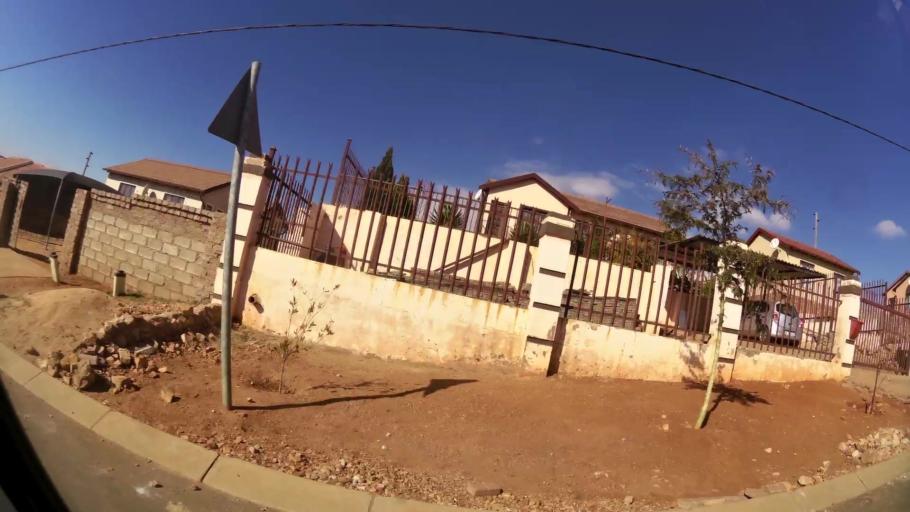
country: ZA
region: Gauteng
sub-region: City of Tshwane Metropolitan Municipality
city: Cullinan
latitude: -25.6930
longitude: 28.4153
